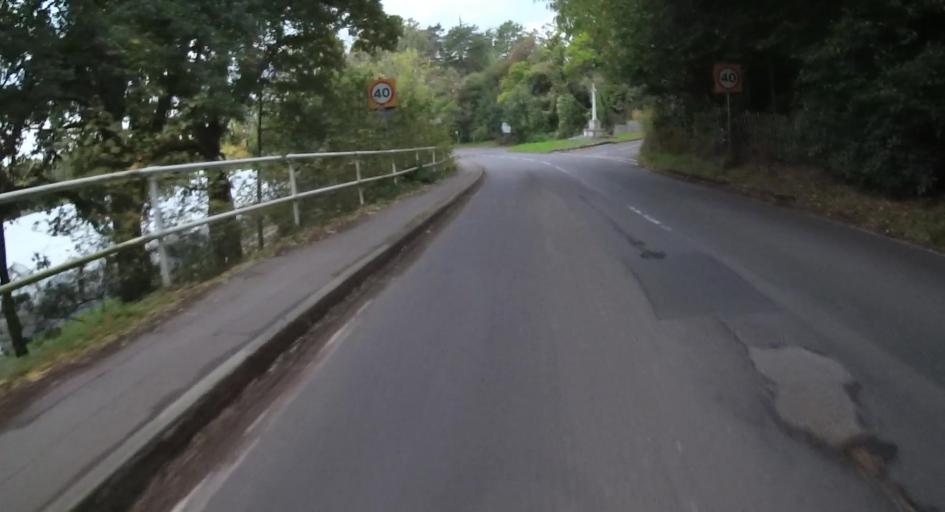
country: GB
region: England
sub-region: Wokingham
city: Finchampstead
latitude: 51.3659
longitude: -0.8527
